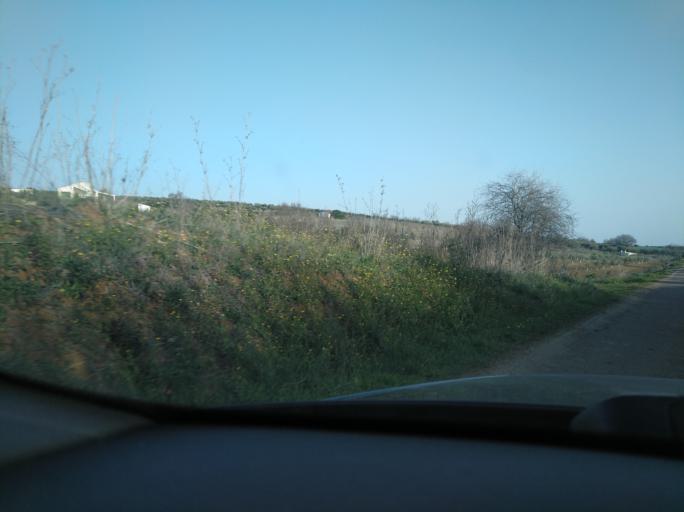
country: PT
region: Portalegre
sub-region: Campo Maior
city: Campo Maior
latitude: 39.0057
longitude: -7.0169
